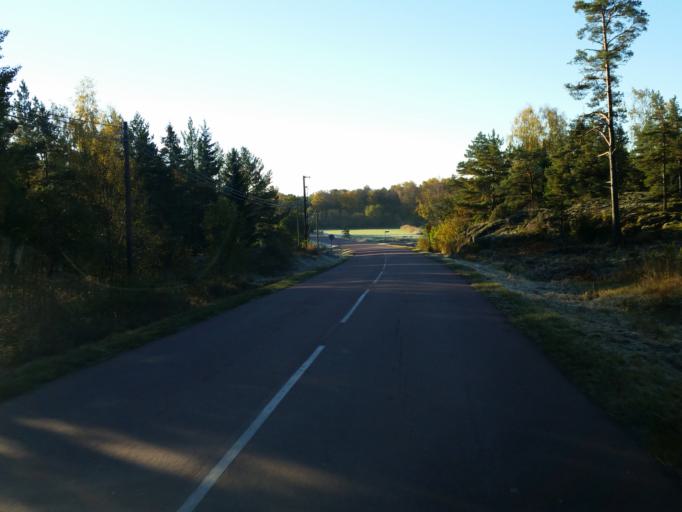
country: AX
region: Alands skaergard
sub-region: Vardoe
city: Vardoe
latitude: 60.2497
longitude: 20.3710
